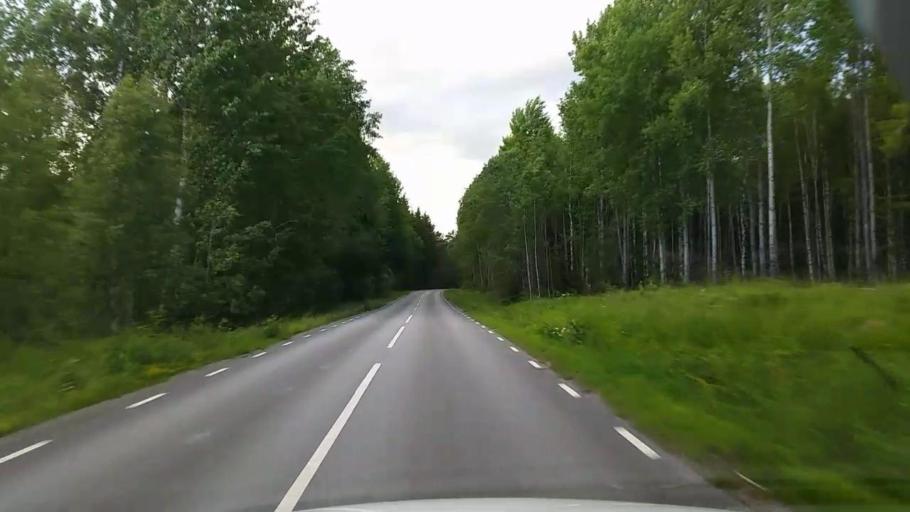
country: SE
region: Vaestmanland
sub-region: Kopings Kommun
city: Kolsva
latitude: 59.7540
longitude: 15.8327
